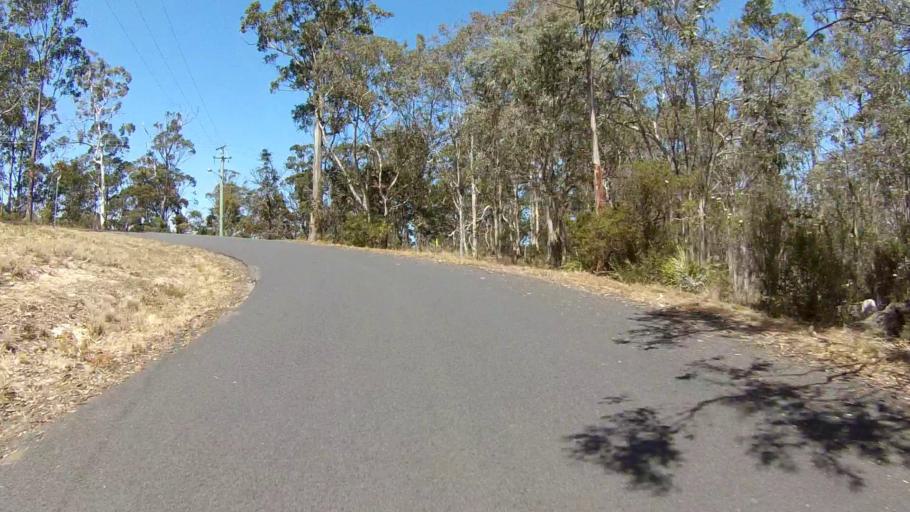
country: AU
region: Tasmania
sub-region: Clarence
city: Sandford
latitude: -43.0139
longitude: 147.4800
